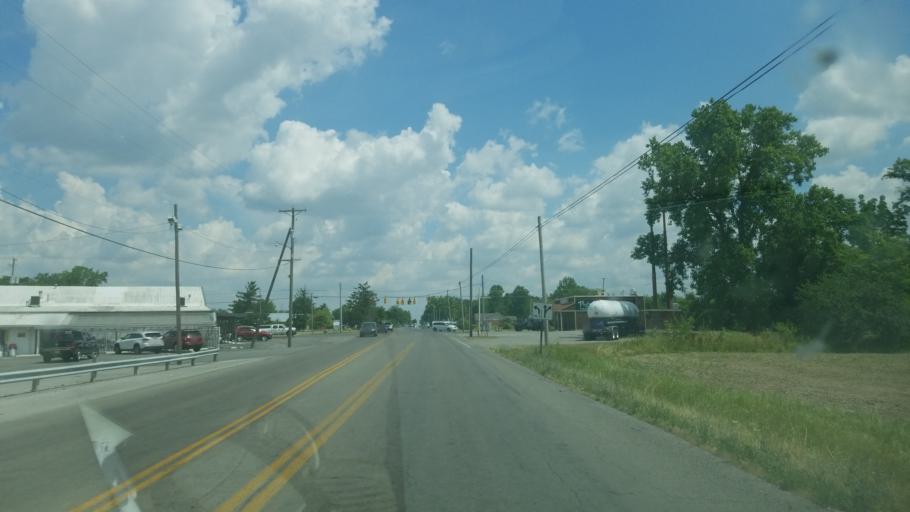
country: US
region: Ohio
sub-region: Allen County
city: Fort Shawnee
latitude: 40.6857
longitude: -84.1291
